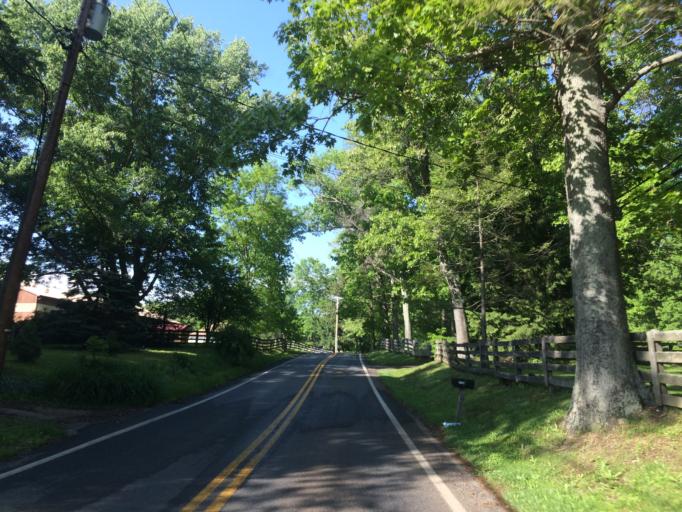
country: US
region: Maryland
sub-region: Carroll County
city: Sykesville
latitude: 39.2853
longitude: -76.9349
